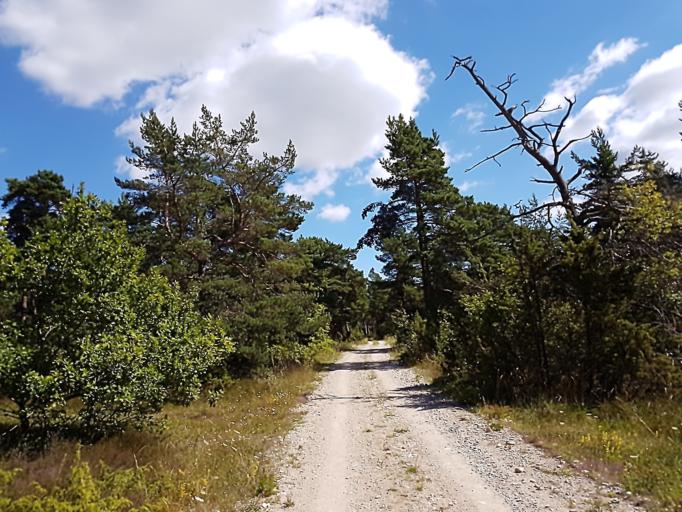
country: SE
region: Gotland
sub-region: Gotland
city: Visby
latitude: 57.6078
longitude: 18.3362
